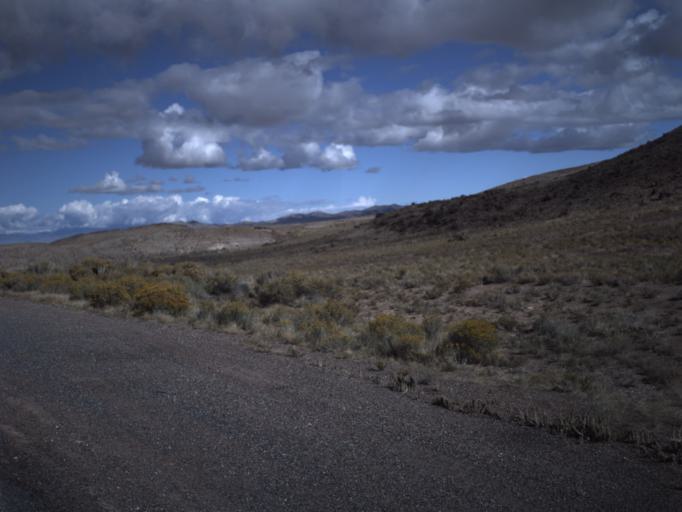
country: US
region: Utah
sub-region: Beaver County
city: Milford
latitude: 38.6167
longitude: -113.8438
